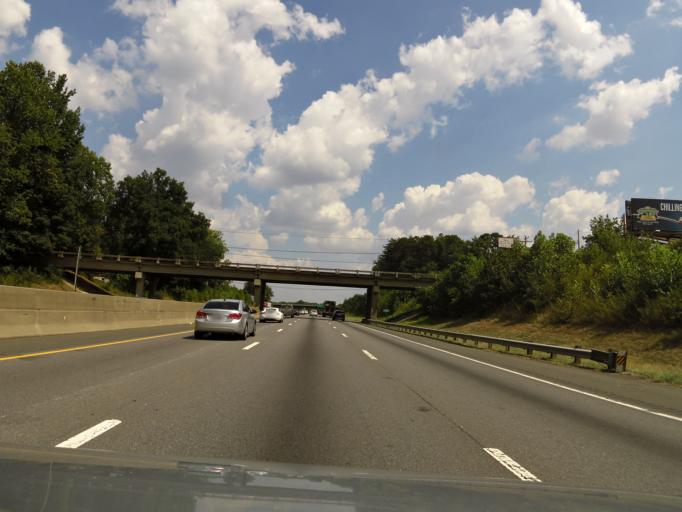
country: US
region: North Carolina
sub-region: Gaston County
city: Lowell
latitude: 35.2610
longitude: -81.1102
